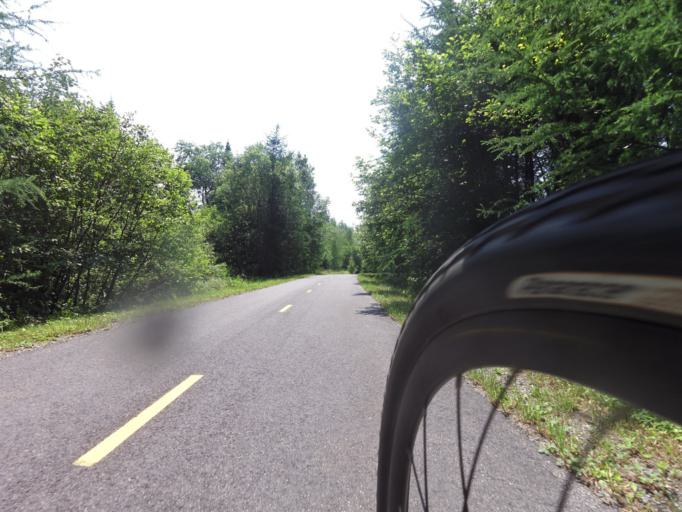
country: CA
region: Quebec
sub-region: Laurentides
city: Mont-Tremblant
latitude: 46.1455
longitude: -74.5935
